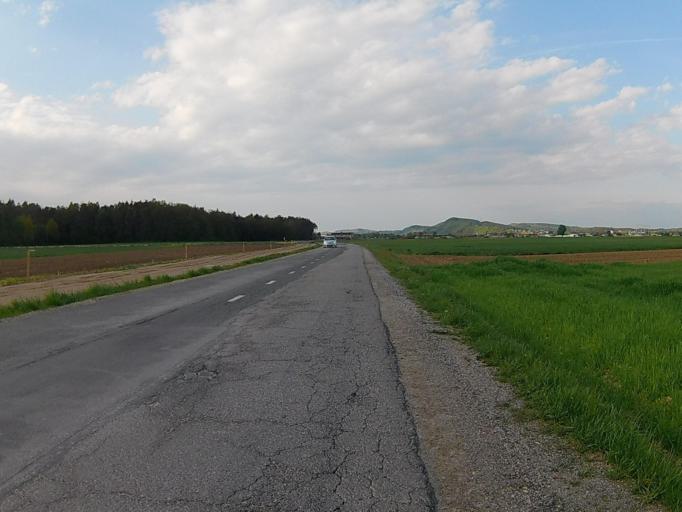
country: SI
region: Miklavz na Dravskem Polju
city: Miklavz na Dravskem Polju
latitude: 46.4910
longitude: 15.7012
